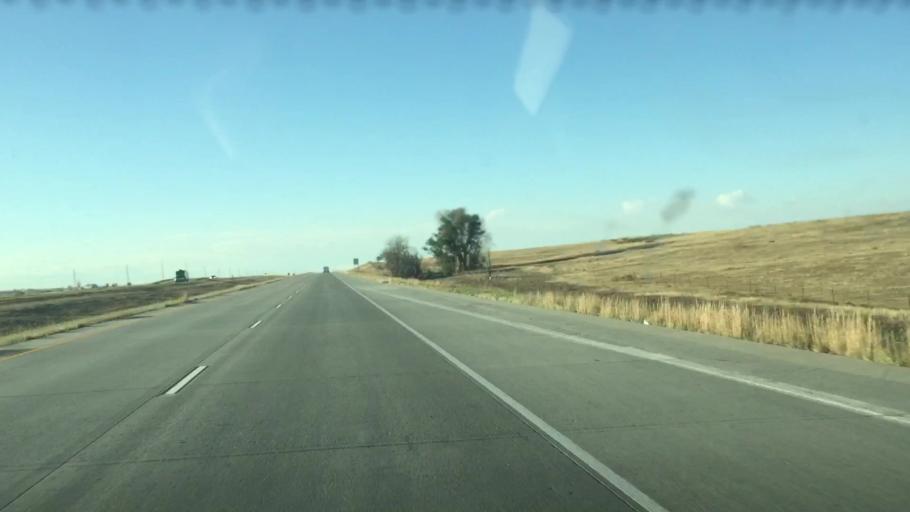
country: US
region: Colorado
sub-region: Arapahoe County
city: Byers
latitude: 39.5735
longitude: -104.0186
